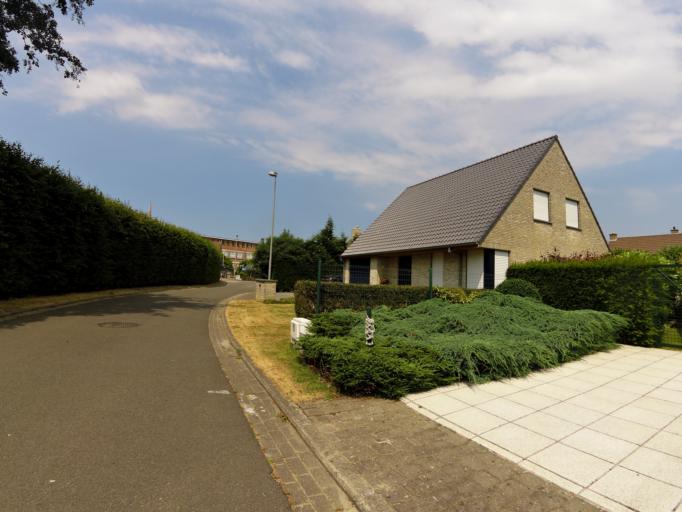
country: BE
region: Flanders
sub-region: Provincie West-Vlaanderen
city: Oudenburg
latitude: 51.1812
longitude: 3.0056
